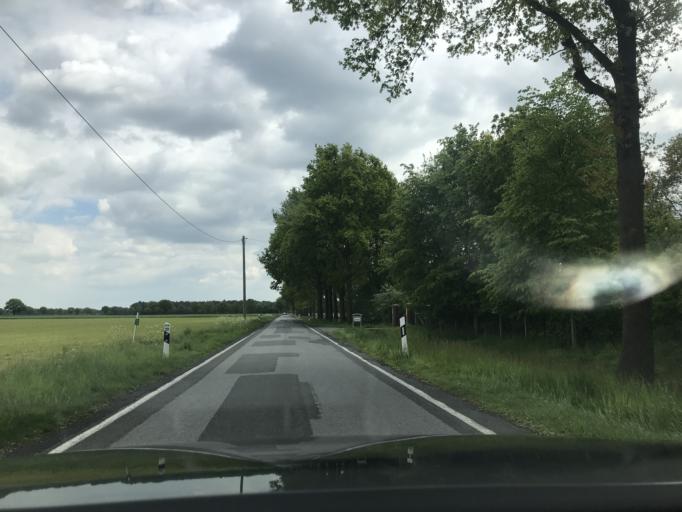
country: DE
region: North Rhine-Westphalia
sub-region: Regierungsbezirk Detmold
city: Harsewinkel
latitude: 51.9178
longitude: 8.2130
